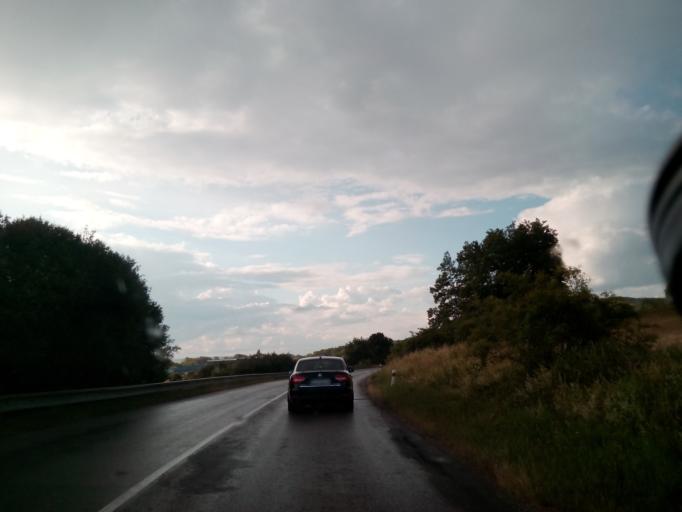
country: SK
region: Kosicky
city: Kosice
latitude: 48.6519
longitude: 21.3602
